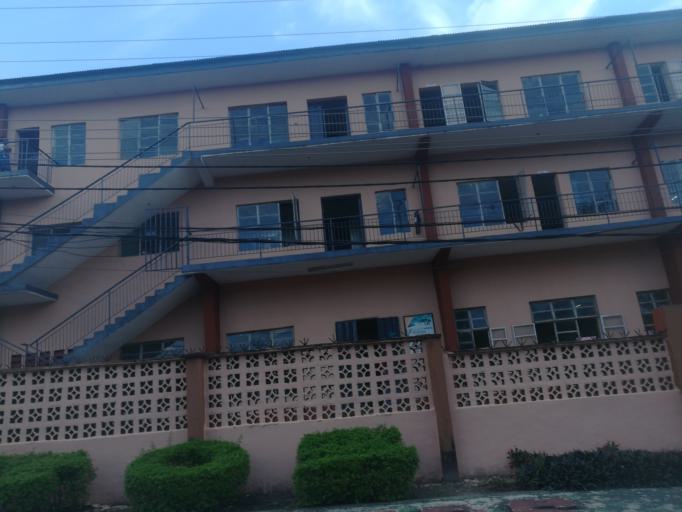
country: NG
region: Lagos
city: Ojota
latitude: 6.5632
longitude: 3.3748
